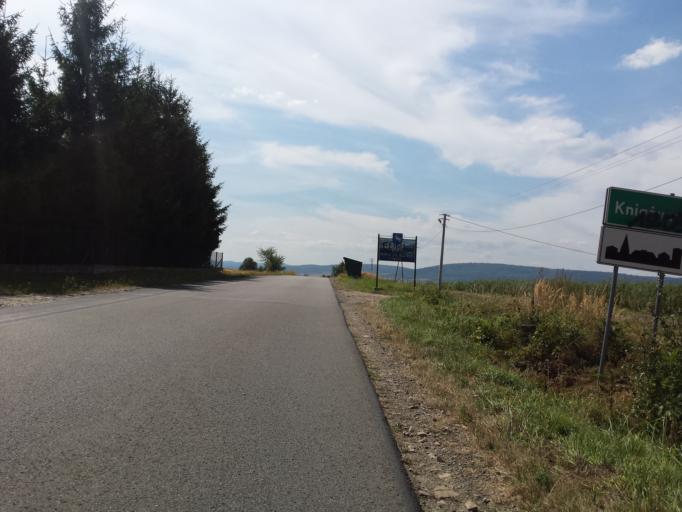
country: PL
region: Subcarpathian Voivodeship
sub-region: Powiat przemyski
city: Fredropol
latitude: 49.7206
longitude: 22.7603
